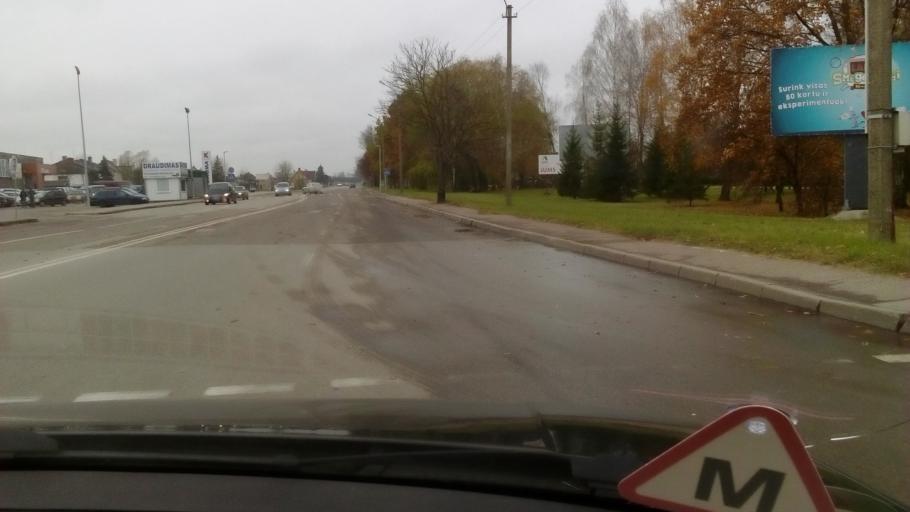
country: LT
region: Marijampoles apskritis
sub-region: Marijampole Municipality
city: Marijampole
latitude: 54.5537
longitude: 23.3743
